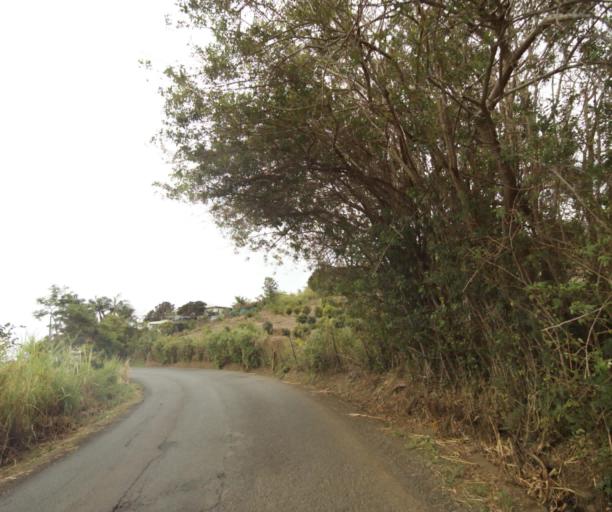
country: RE
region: Reunion
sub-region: Reunion
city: Saint-Paul
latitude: -21.0357
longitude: 55.2902
